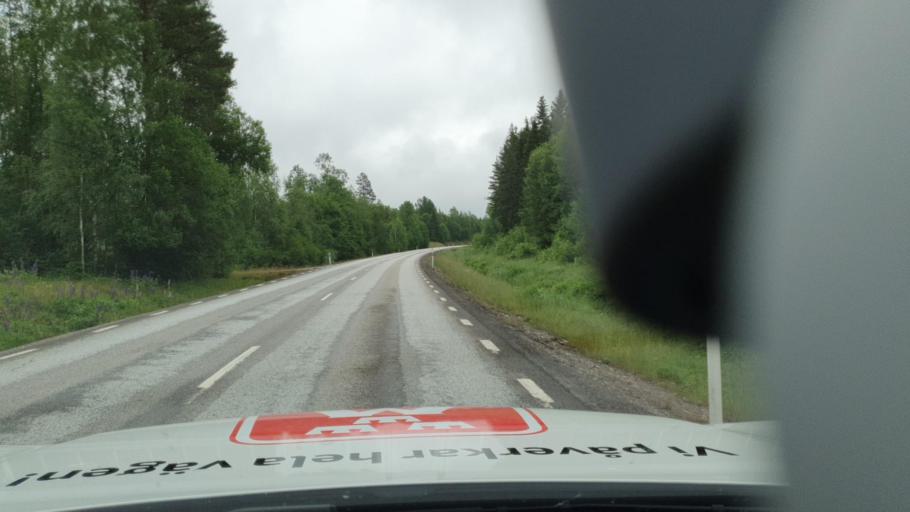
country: SE
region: Vaermland
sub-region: Kristinehamns Kommun
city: Bjorneborg
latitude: 59.2509
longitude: 14.2059
